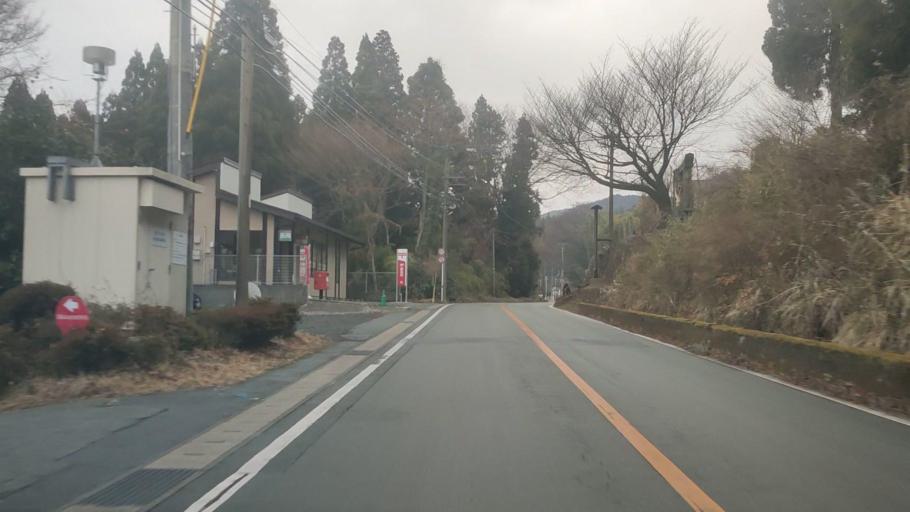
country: JP
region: Kumamoto
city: Aso
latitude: 32.8562
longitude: 131.1579
